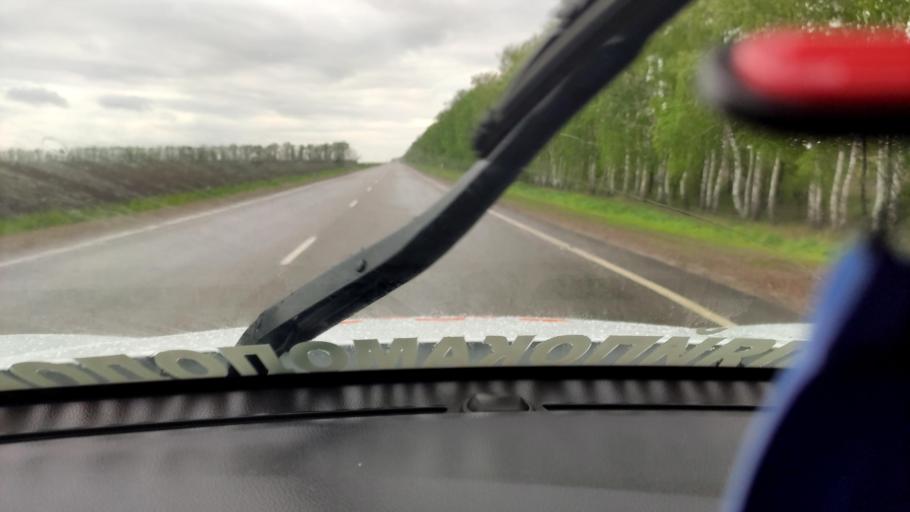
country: RU
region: Voronezj
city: Sredniy Ikorets
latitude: 51.0394
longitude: 39.6624
